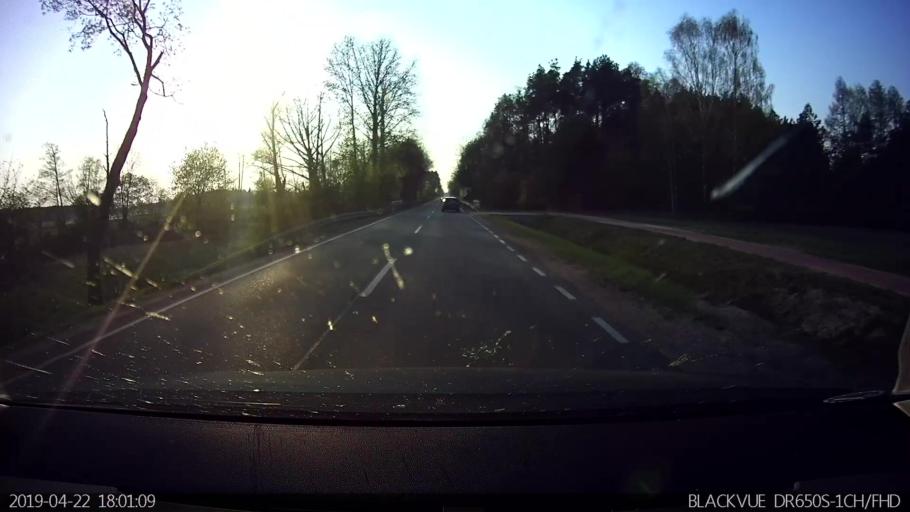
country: PL
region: Masovian Voivodeship
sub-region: Powiat wegrowski
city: Korytnica
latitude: 52.4778
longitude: 21.8347
